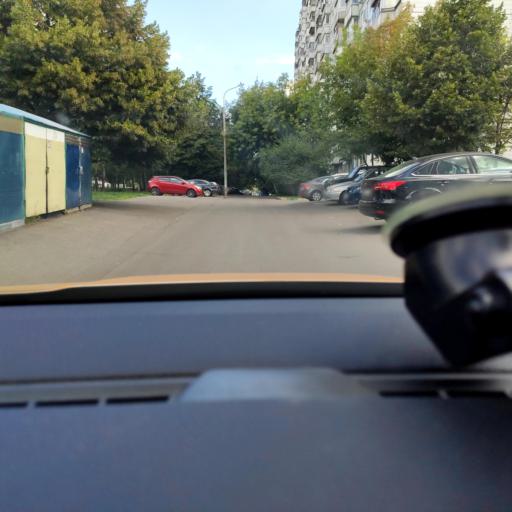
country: RU
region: Moscow
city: Businovo
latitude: 55.8894
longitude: 37.5223
